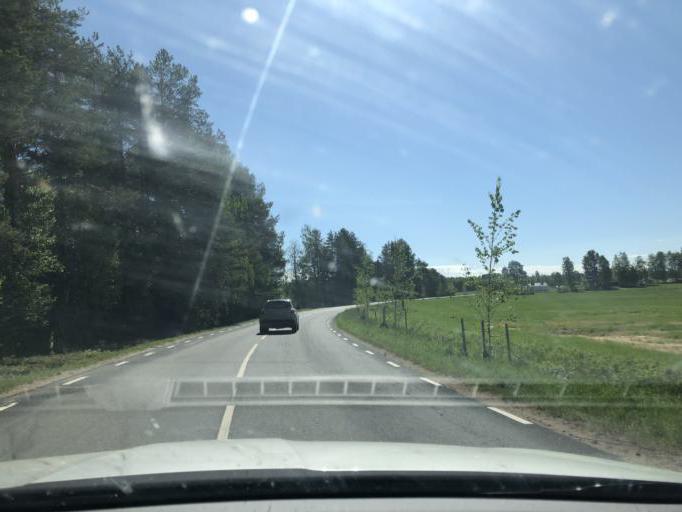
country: SE
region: Norrbotten
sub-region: Lulea Kommun
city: Gammelstad
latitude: 65.6553
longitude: 22.0135
